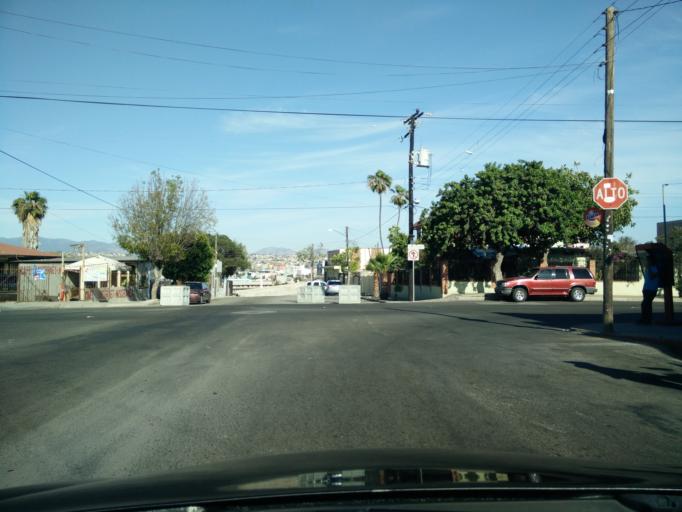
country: MX
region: Baja California
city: Tijuana
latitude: 32.5251
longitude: -117.0396
